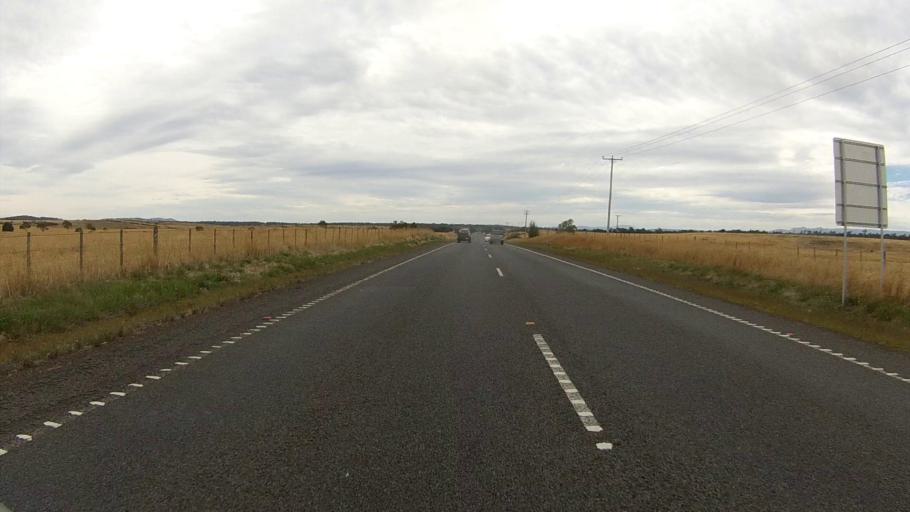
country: AU
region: Tasmania
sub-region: Northern Midlands
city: Evandale
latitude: -41.8629
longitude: 147.4566
